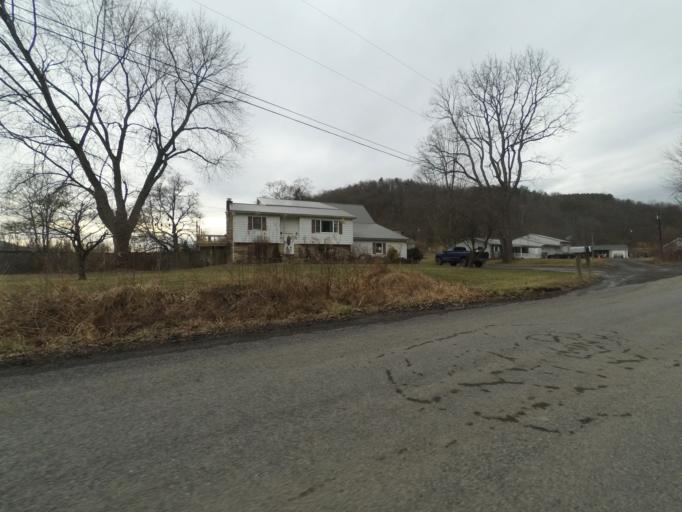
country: US
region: Pennsylvania
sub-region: Centre County
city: Stormstown
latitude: 40.8464
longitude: -77.9855
